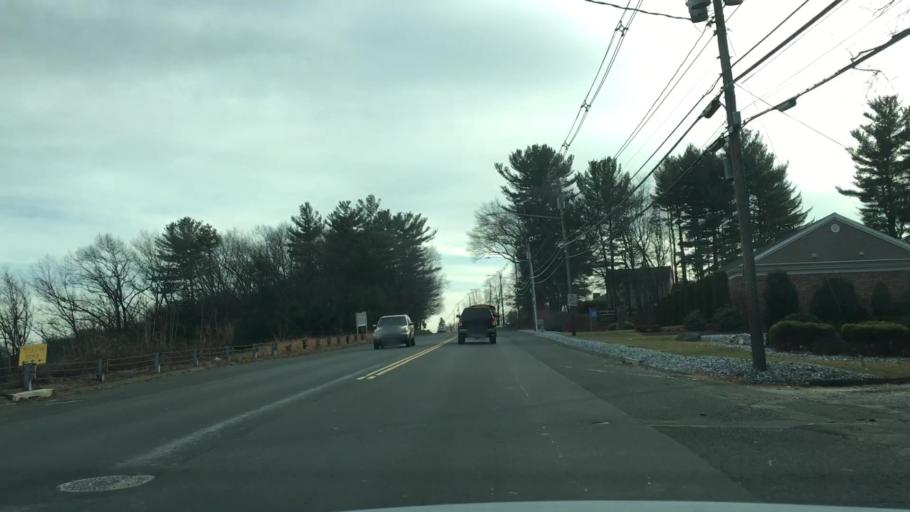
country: US
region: Massachusetts
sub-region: Hampden County
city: Westfield
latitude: 42.1071
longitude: -72.7647
